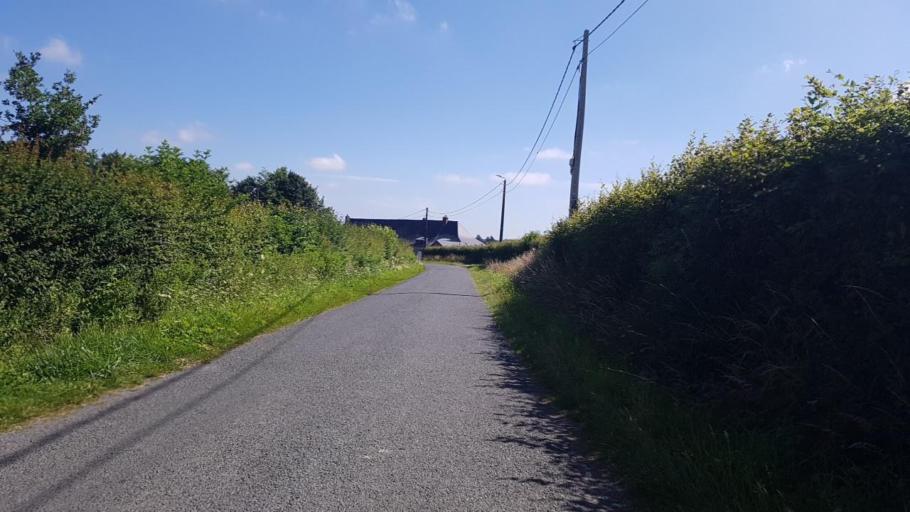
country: BE
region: Wallonia
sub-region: Province du Hainaut
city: Momignies
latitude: 50.0122
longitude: 4.1496
